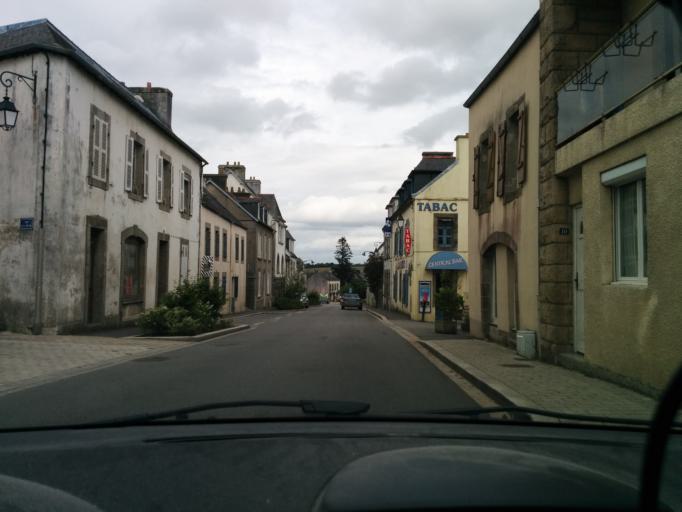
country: FR
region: Brittany
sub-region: Departement du Finistere
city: Pleyben
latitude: 48.2273
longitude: -3.9691
